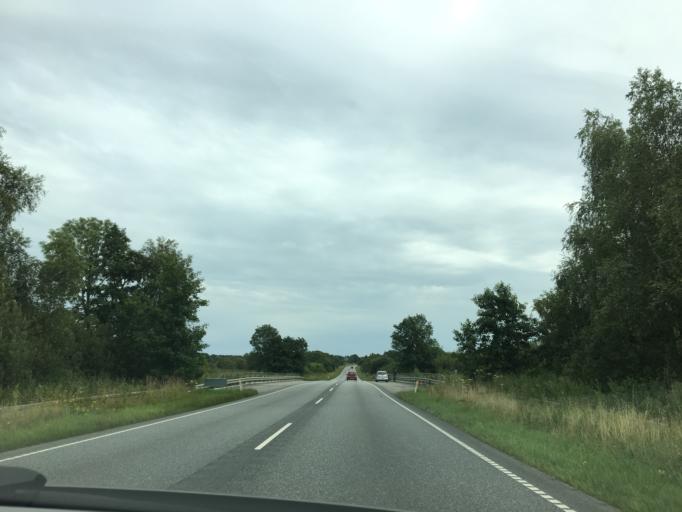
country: DK
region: South Denmark
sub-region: Fredericia Kommune
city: Fredericia
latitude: 55.6222
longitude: 9.7389
